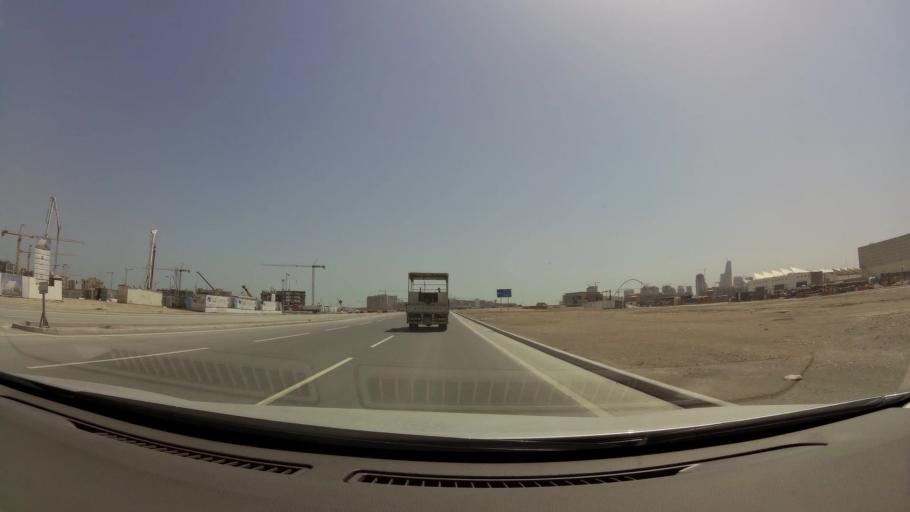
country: QA
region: Baladiyat Umm Salal
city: Umm Salal Muhammad
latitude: 25.4068
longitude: 51.5045
